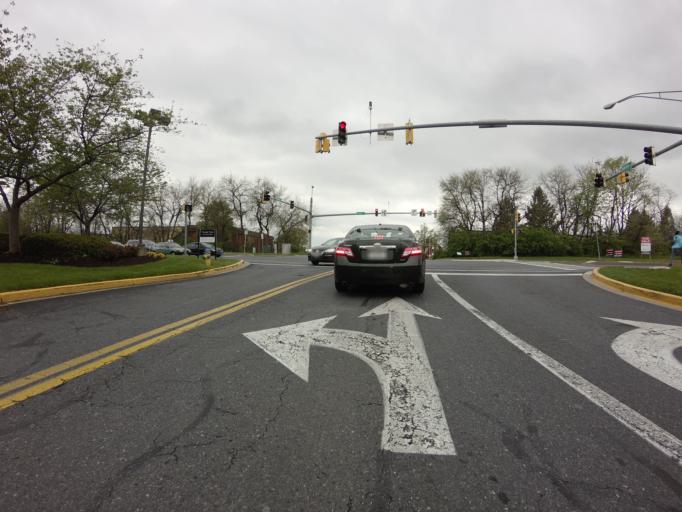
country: US
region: Maryland
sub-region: Frederick County
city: Frederick
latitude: 39.3946
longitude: -77.4162
